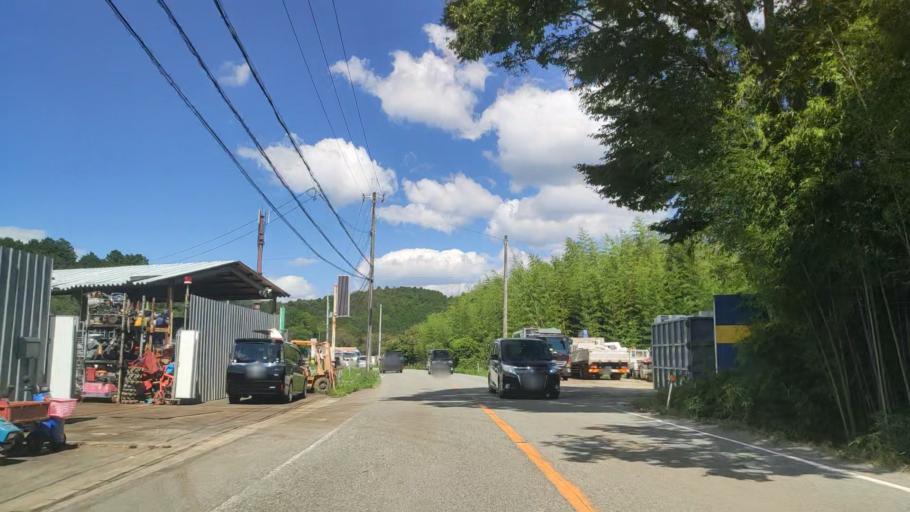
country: JP
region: Kyoto
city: Fukuchiyama
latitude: 35.1847
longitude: 135.1239
